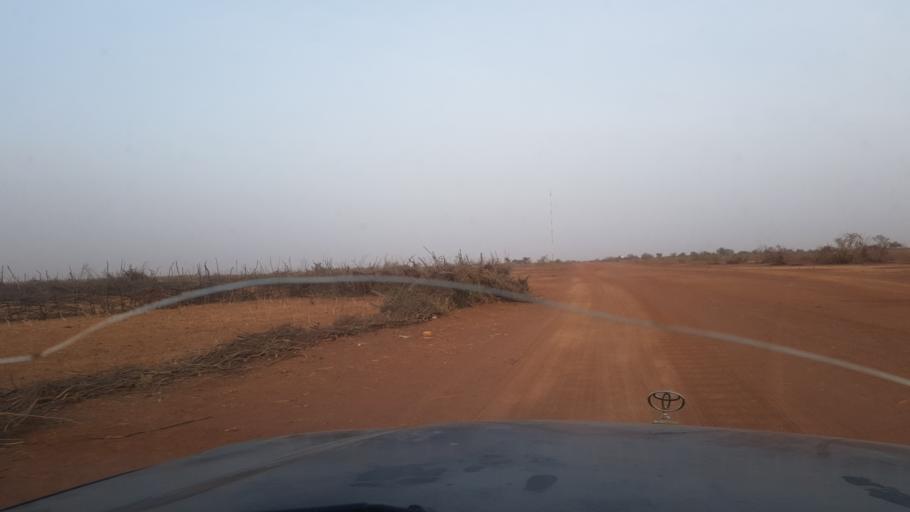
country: NE
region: Niamey
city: Niamey
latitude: 13.4286
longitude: 1.9707
